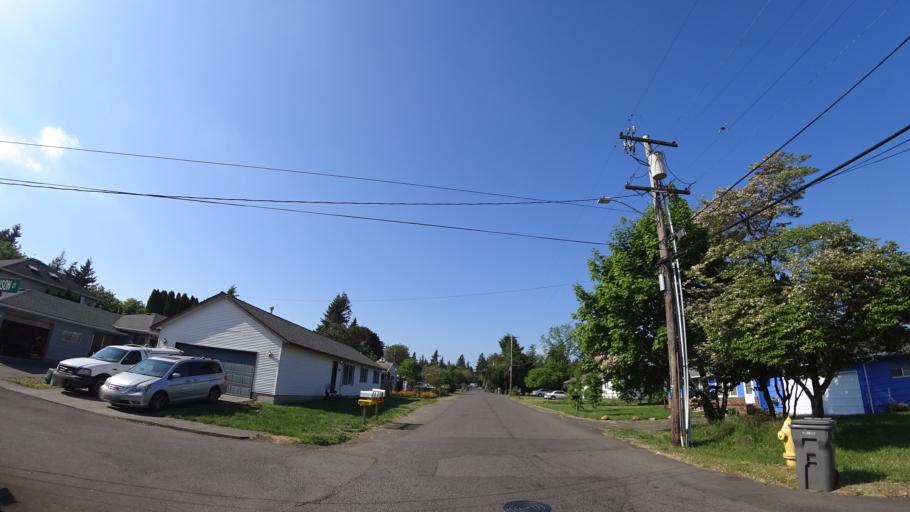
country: US
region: Oregon
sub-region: Multnomah County
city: Lents
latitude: 45.5166
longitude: -122.5081
